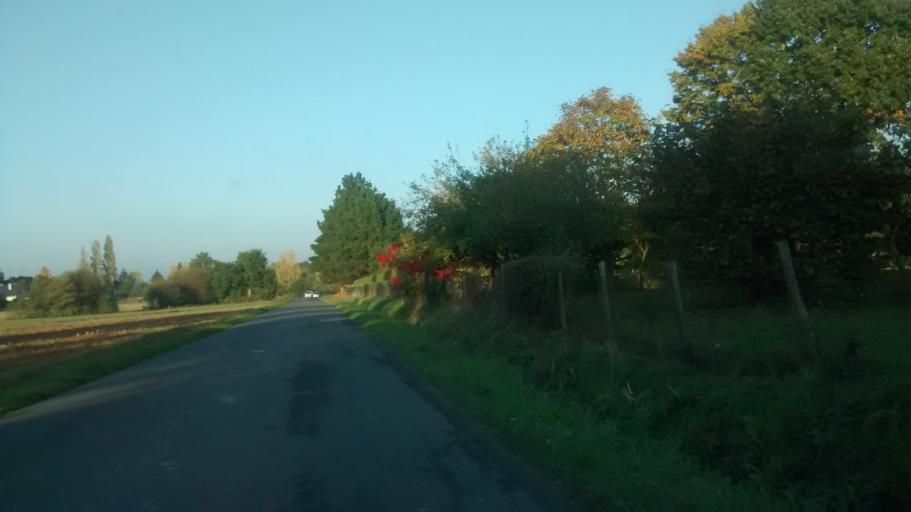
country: FR
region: Brittany
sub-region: Departement d'Ille-et-Vilaine
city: La Chapelle-Thouarault
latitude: 48.1173
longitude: -1.8390
